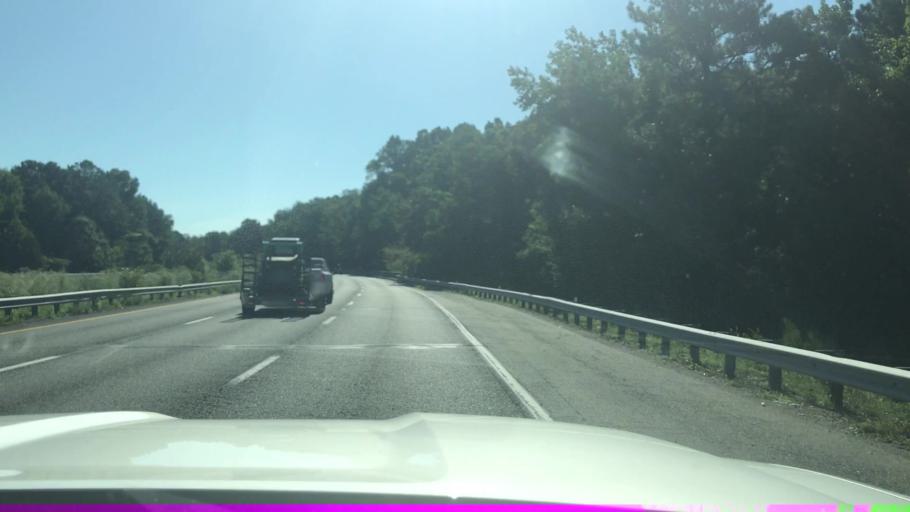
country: US
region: Virginia
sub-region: Henrico County
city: Montrose
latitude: 37.5302
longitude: -77.3751
